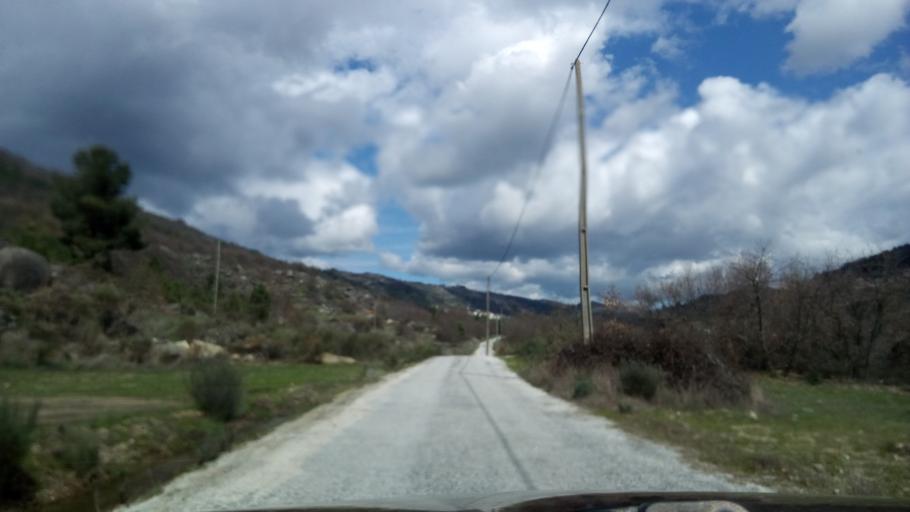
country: PT
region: Guarda
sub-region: Fornos de Algodres
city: Fornos de Algodres
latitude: 40.6442
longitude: -7.5068
